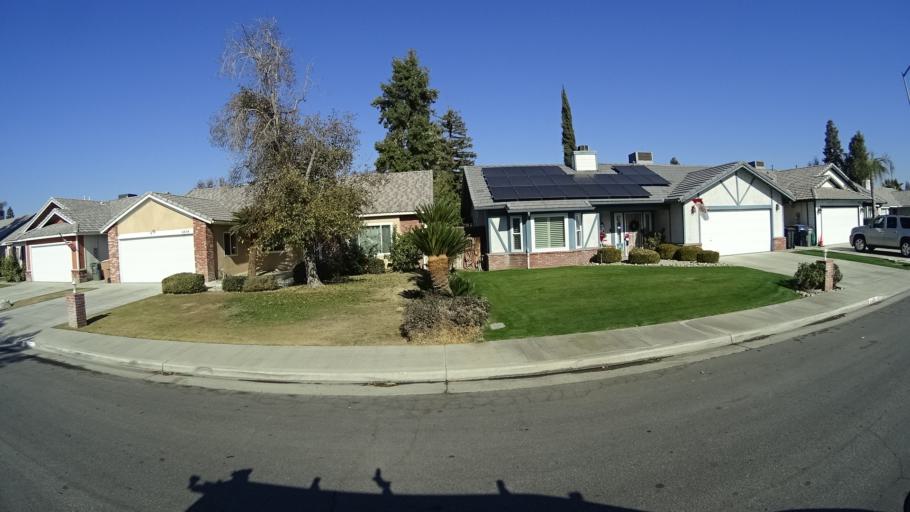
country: US
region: California
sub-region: Kern County
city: Greenfield
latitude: 35.2930
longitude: -119.0513
